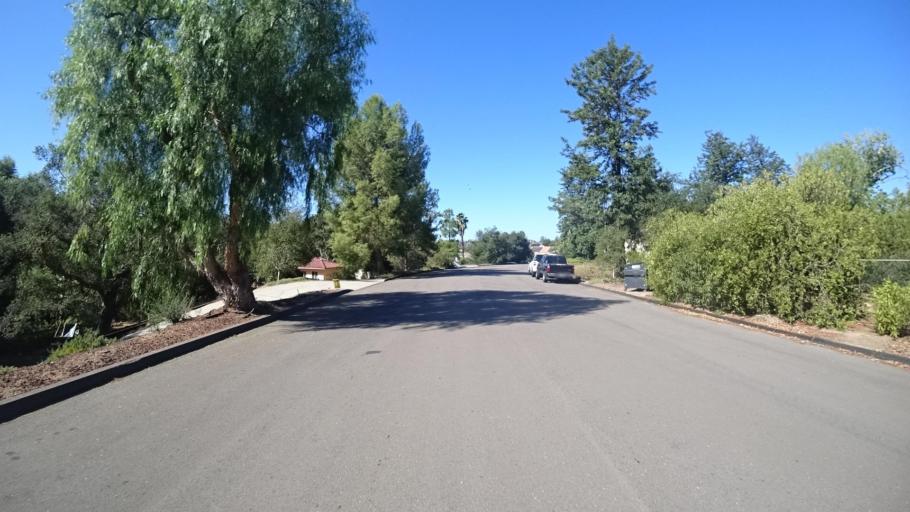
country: US
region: California
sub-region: San Diego County
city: San Diego Country Estates
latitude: 33.0054
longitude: -116.7899
